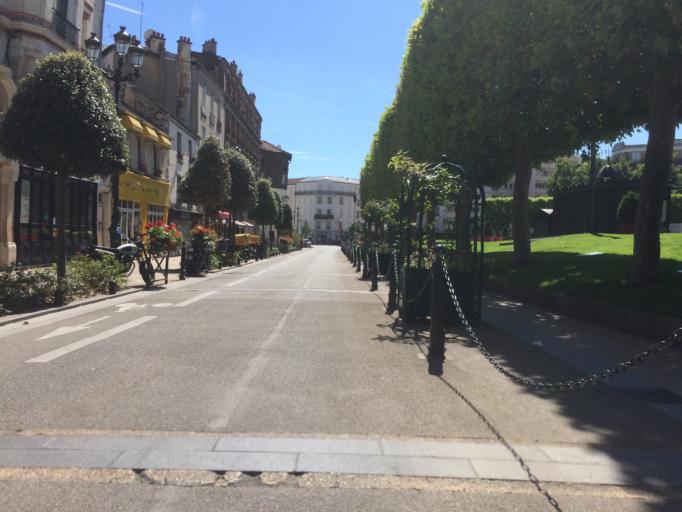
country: FR
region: Ile-de-France
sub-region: Departement des Hauts-de-Seine
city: Puteaux
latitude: 48.8838
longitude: 2.2395
